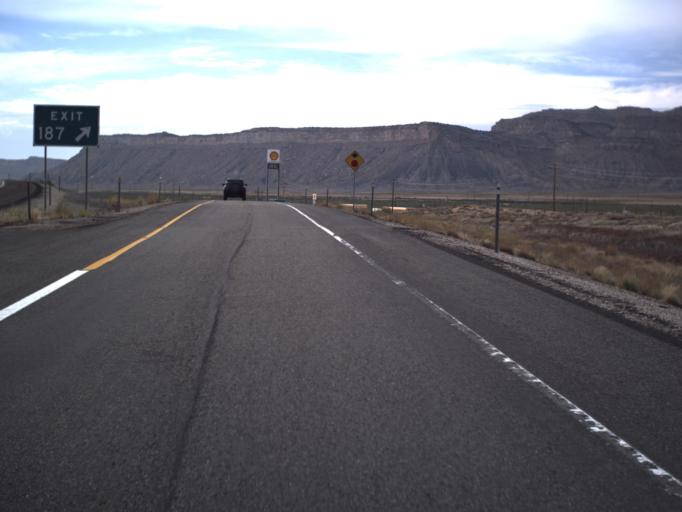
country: US
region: Utah
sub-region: Grand County
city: Moab
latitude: 38.9620
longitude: -109.7174
